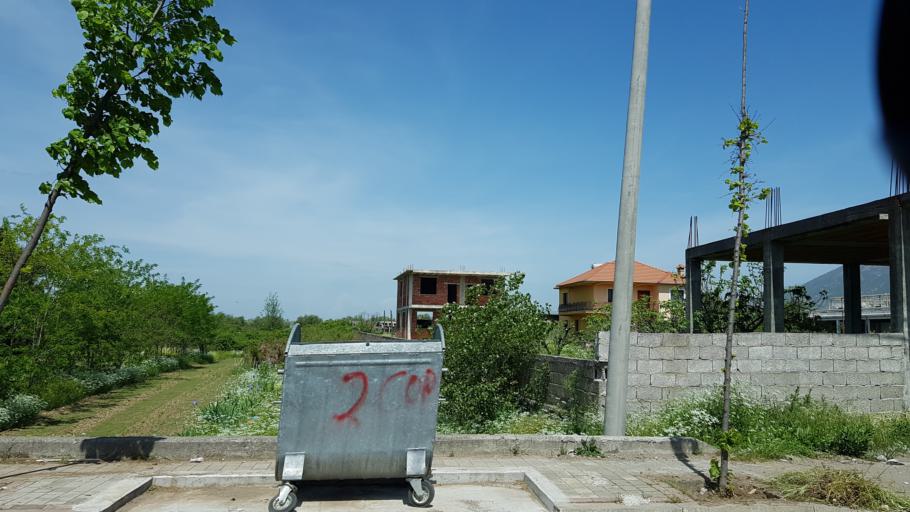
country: AL
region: Shkoder
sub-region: Rrethi i Shkodres
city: Guri i Zi
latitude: 42.1102
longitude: 19.5669
